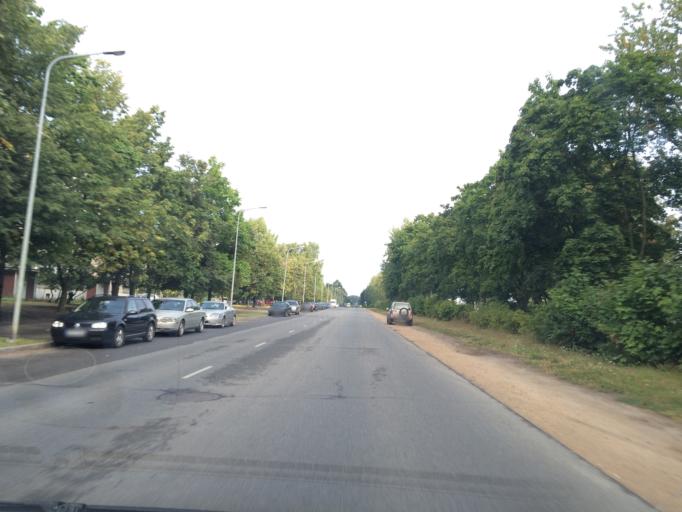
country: LV
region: Kekava
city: Kekava
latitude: 56.9061
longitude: 24.2073
